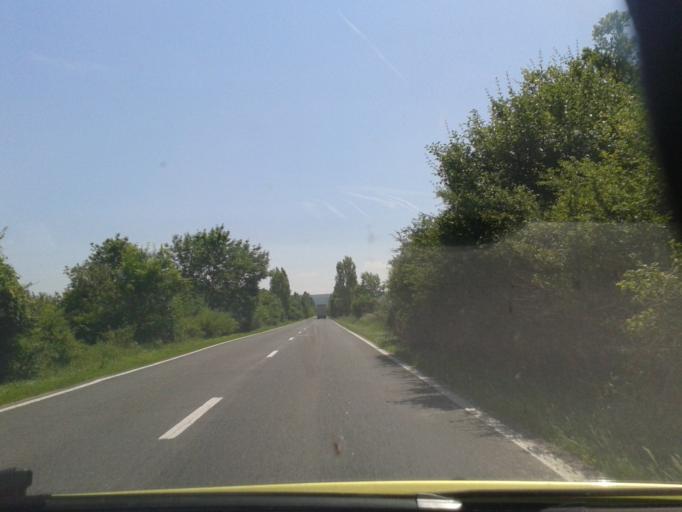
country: RO
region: Timis
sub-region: Comuna Margina
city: Margina
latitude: 45.8521
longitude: 22.2918
